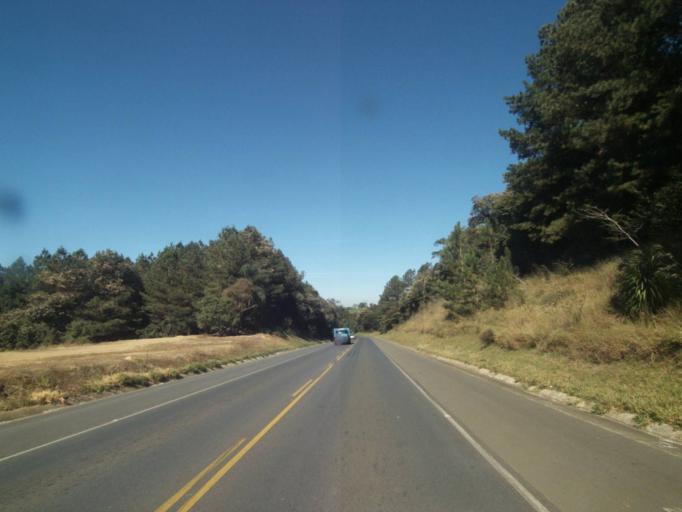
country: BR
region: Parana
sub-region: Tibagi
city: Tibagi
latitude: -24.5080
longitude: -50.4416
